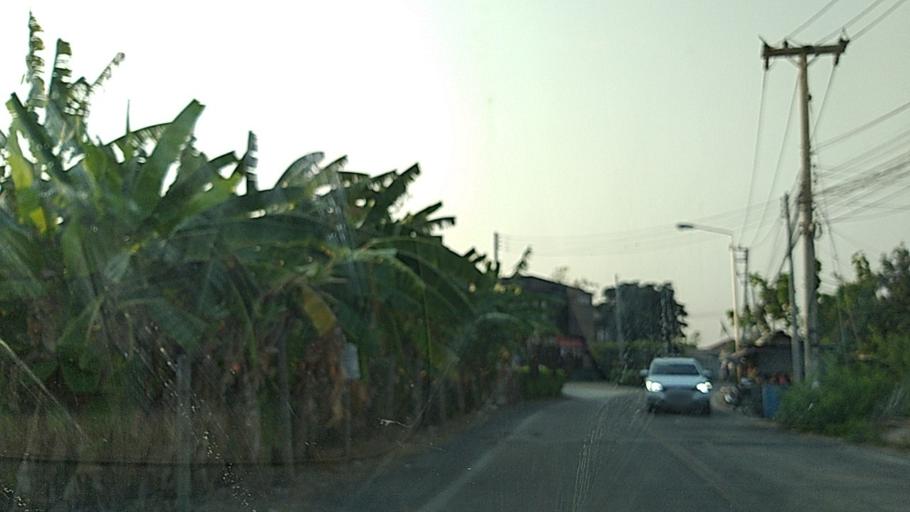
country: TH
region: Phra Nakhon Si Ayutthaya
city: Ban Bang Kadi Pathum Thani
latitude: 13.9948
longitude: 100.5647
